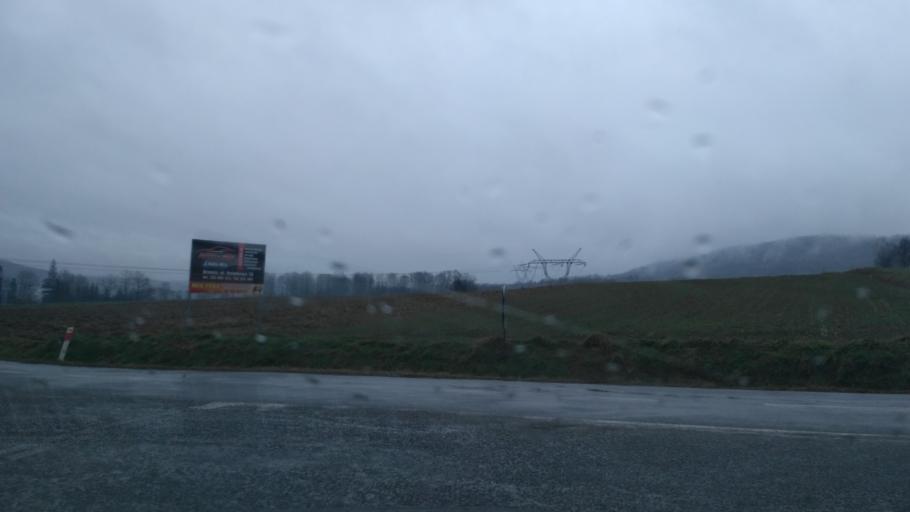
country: PL
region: Subcarpathian Voivodeship
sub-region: Powiat strzyzowski
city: Jawornik
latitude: 49.8035
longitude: 21.8662
